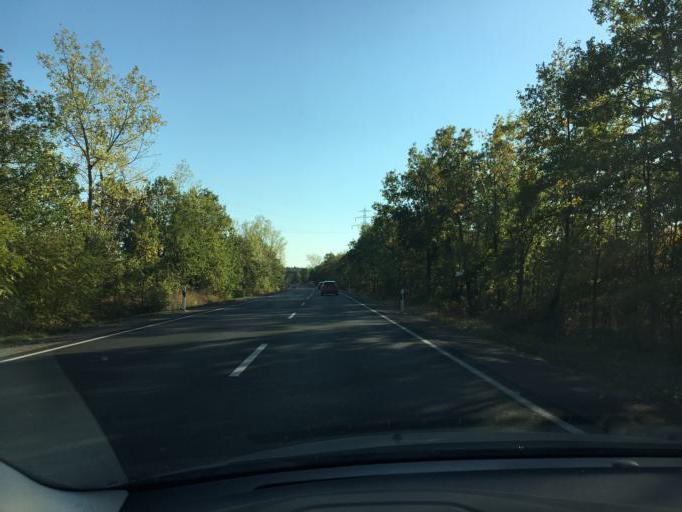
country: DE
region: Saxony-Anhalt
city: Roitzsch
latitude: 51.5756
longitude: 12.2841
